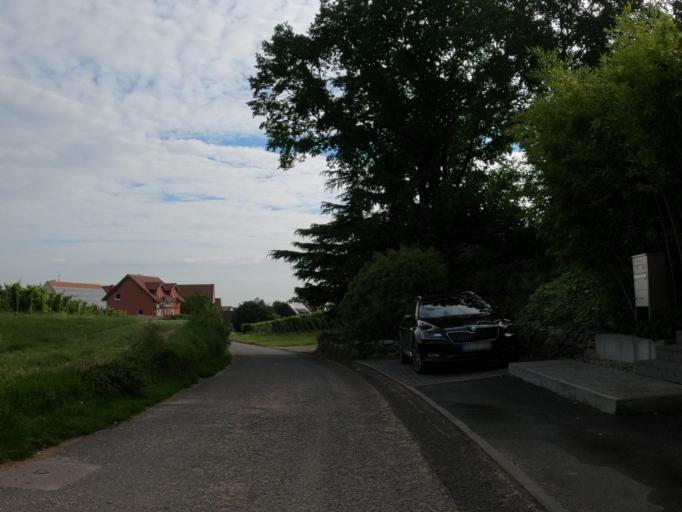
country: DE
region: Rheinland-Pfalz
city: Dackenheim
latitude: 49.5194
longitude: 8.1848
